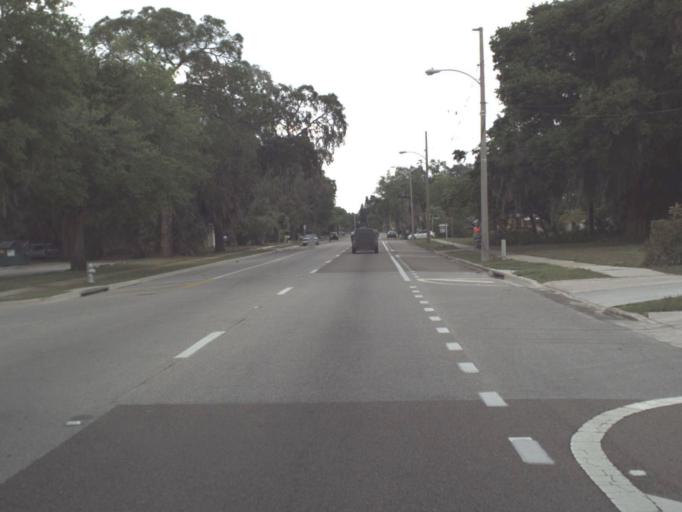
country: US
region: Florida
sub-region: Lake County
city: Eustis
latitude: 28.8581
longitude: -81.6836
